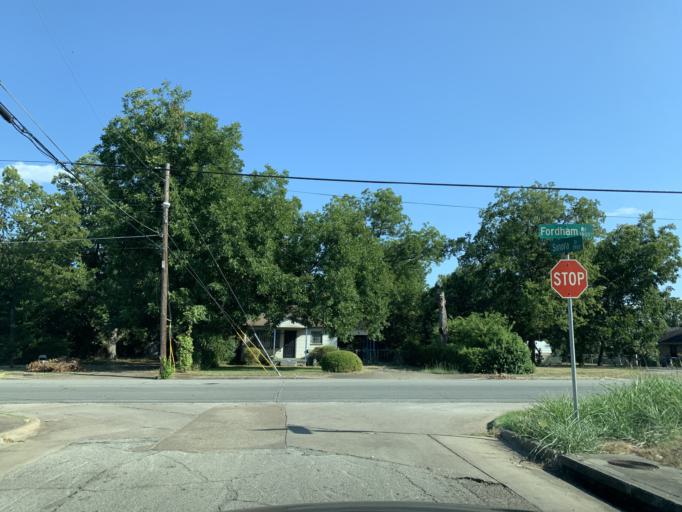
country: US
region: Texas
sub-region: Dallas County
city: Dallas
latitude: 32.7009
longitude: -96.7944
